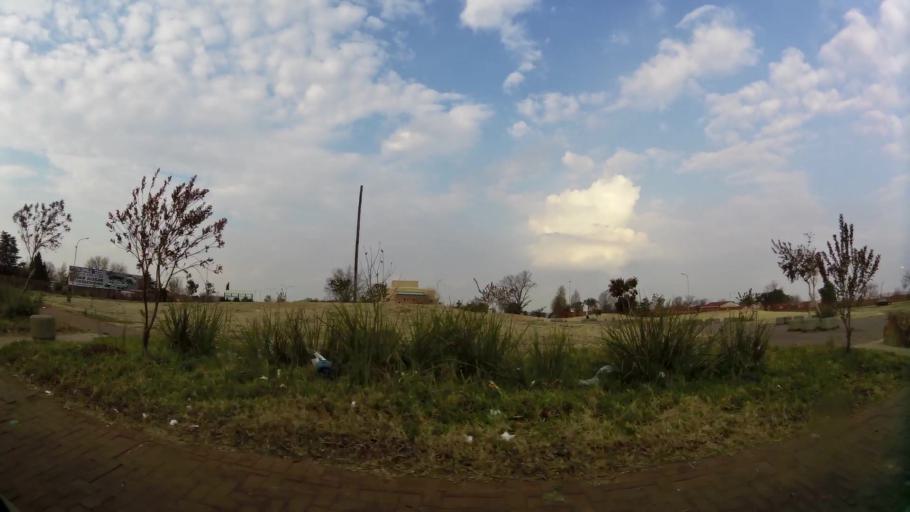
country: ZA
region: Gauteng
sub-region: Sedibeng District Municipality
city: Vanderbijlpark
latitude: -26.6877
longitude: 27.8675
